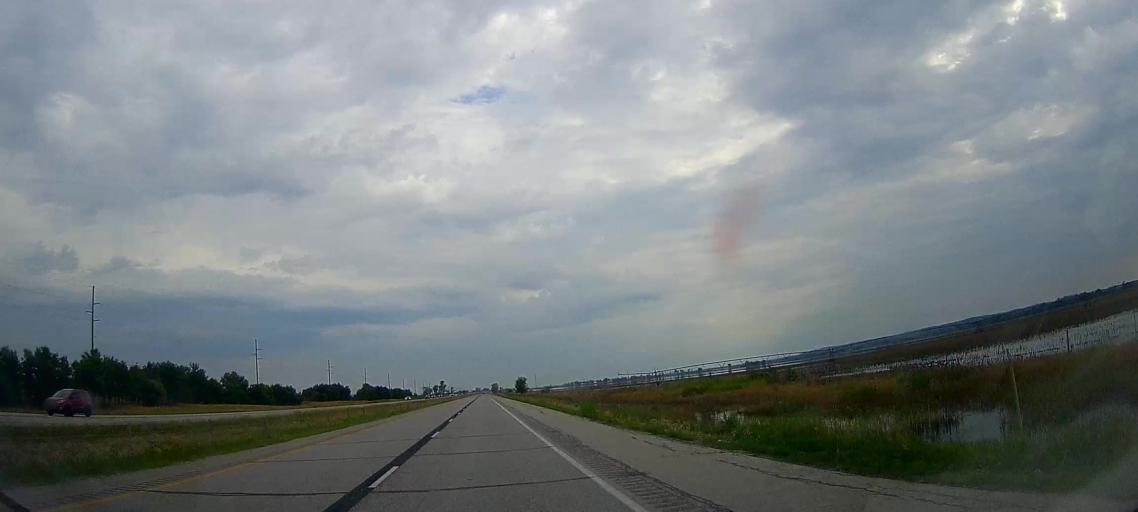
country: US
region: Iowa
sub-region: Harrison County
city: Missouri Valley
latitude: 41.4530
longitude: -95.8999
